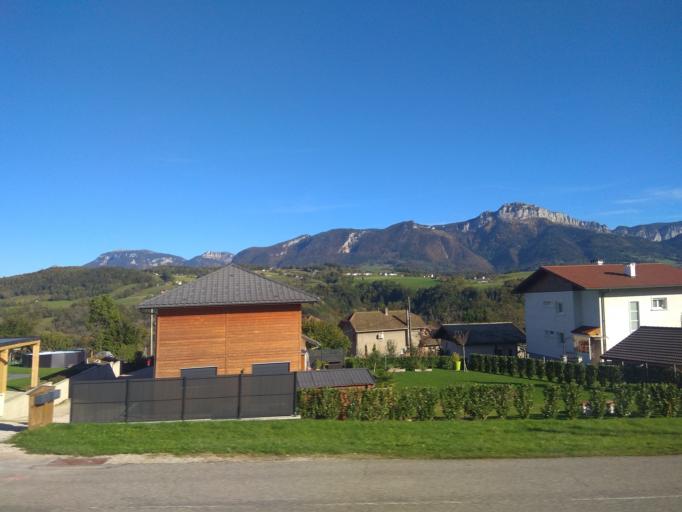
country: FR
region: Rhone-Alpes
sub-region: Departement de la Haute-Savoie
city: Saint-Martin-Bellevue
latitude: 45.9819
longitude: 6.1571
